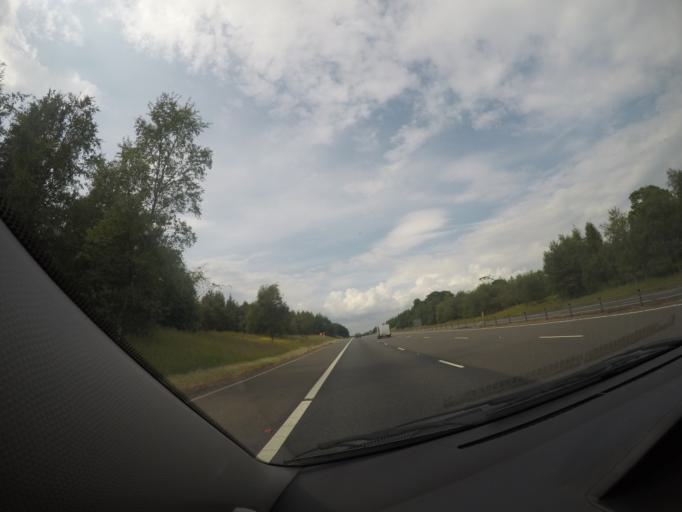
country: GB
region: Scotland
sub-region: Dumfries and Galloway
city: Lockerbie
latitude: 55.1340
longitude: -3.3695
